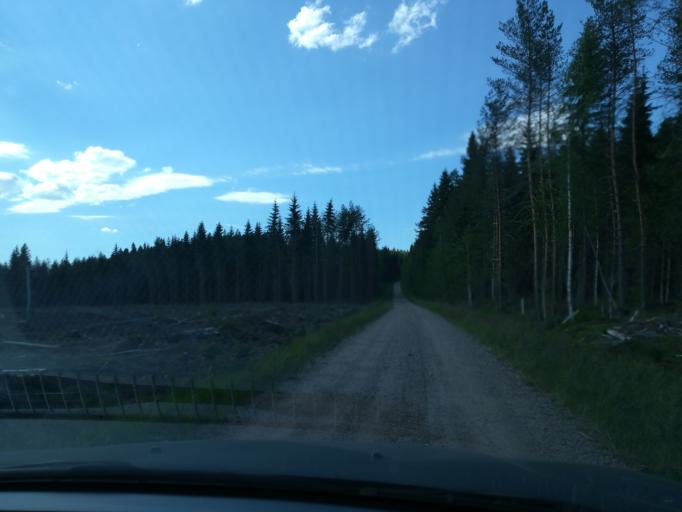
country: FI
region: South Karelia
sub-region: Imatra
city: Ruokolahti
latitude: 61.5397
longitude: 28.8164
